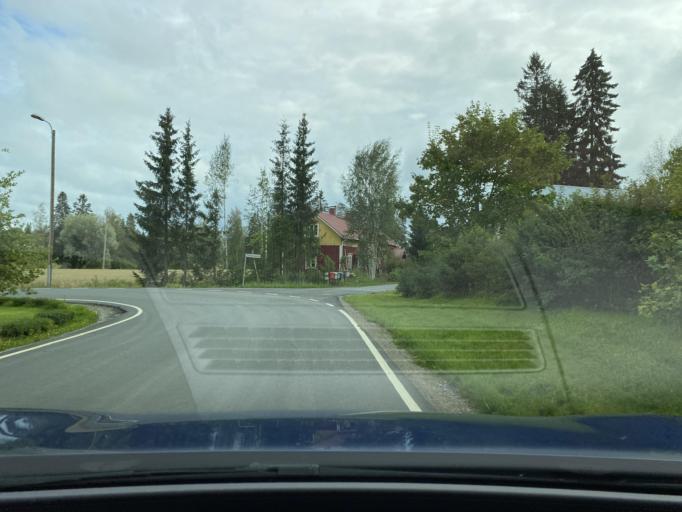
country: FI
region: Pirkanmaa
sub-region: Lounais-Pirkanmaa
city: Punkalaidun
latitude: 61.2321
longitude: 23.1207
